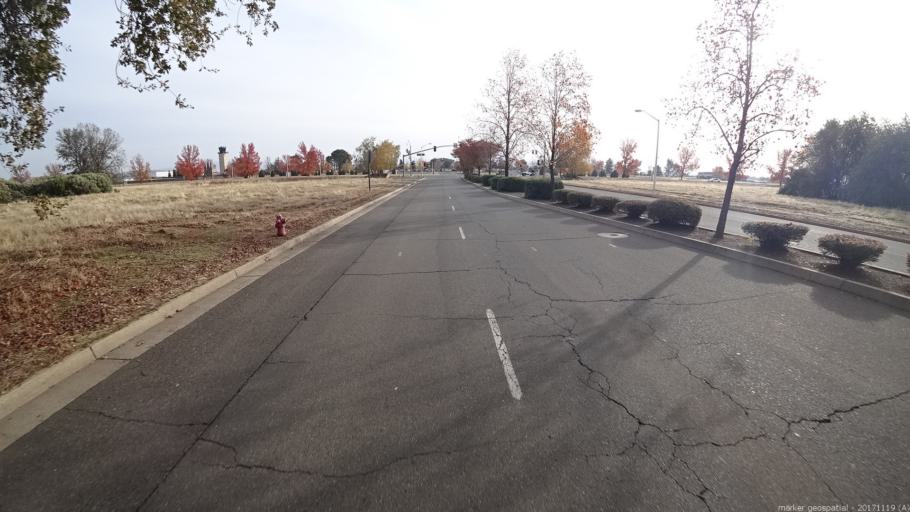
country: US
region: California
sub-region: Shasta County
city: Anderson
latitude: 40.5056
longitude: -122.3037
